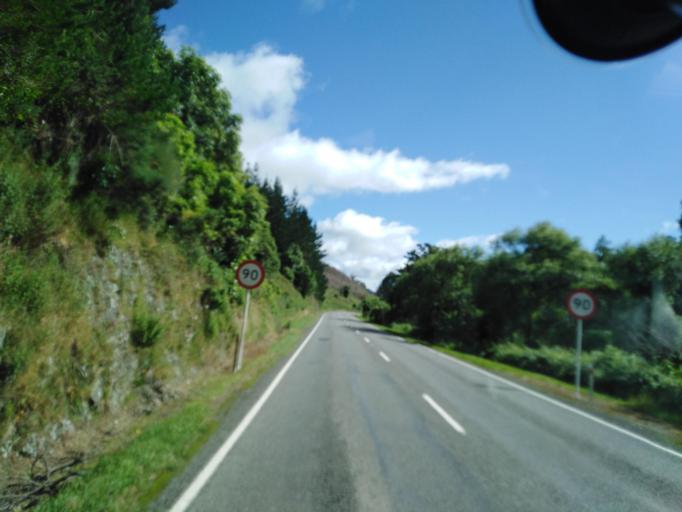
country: NZ
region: Nelson
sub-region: Nelson City
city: Nelson
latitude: -41.2573
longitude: 173.5760
